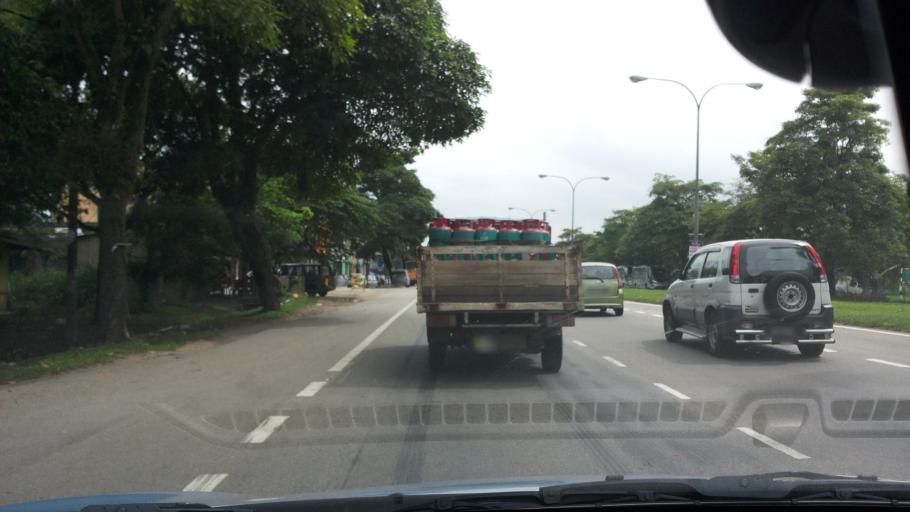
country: MY
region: Pahang
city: Kuantan
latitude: 3.7632
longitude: 103.2153
